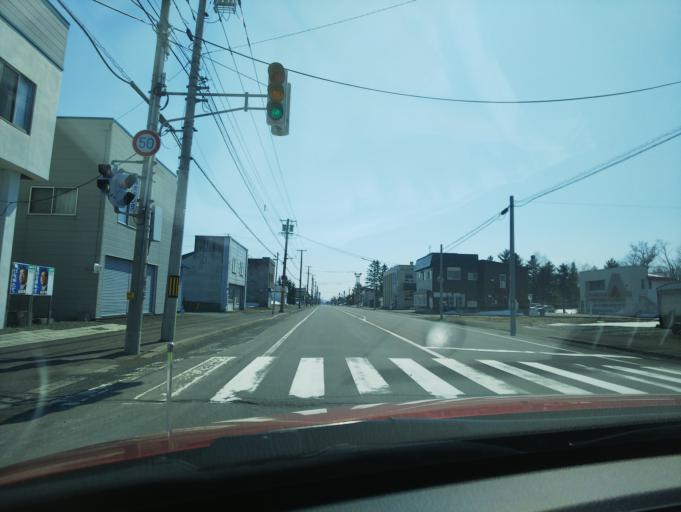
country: JP
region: Hokkaido
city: Nayoro
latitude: 44.2409
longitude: 142.3948
